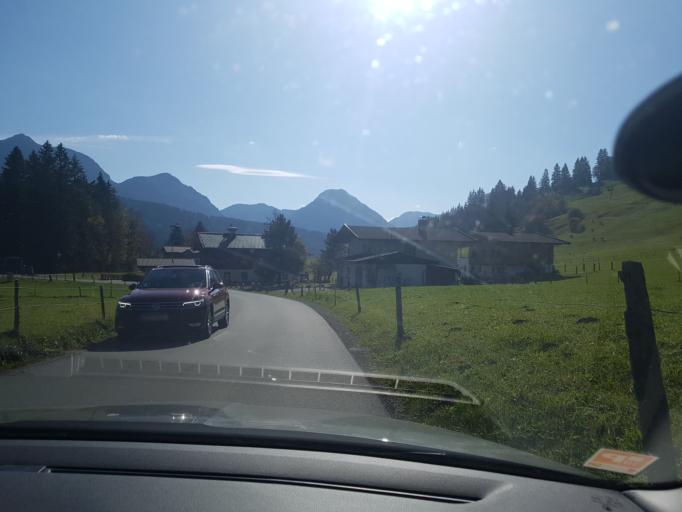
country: AT
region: Tyrol
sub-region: Politischer Bezirk Kitzbuhel
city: Hochfilzen
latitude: 47.4797
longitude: 12.6120
